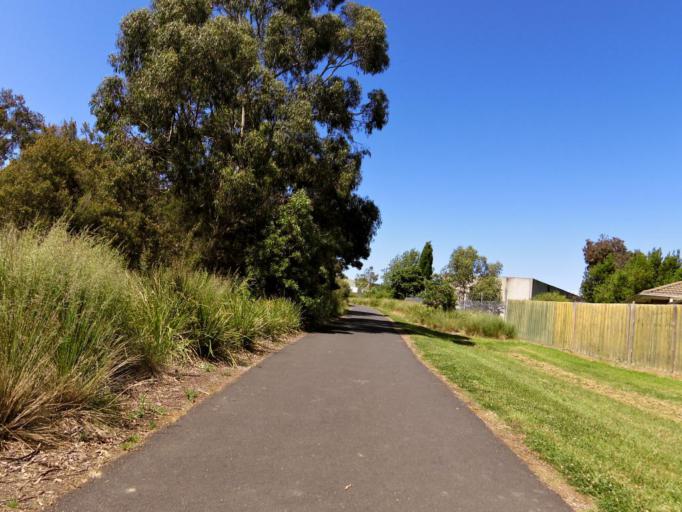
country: AU
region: Victoria
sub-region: Knox
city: Boronia
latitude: -37.8722
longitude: 145.2814
